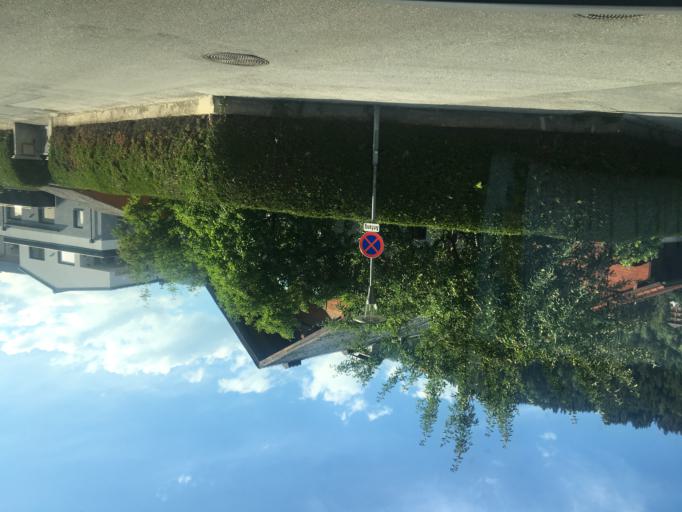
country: AT
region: Styria
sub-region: Politischer Bezirk Liezen
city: Schladming
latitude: 47.3957
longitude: 13.6881
